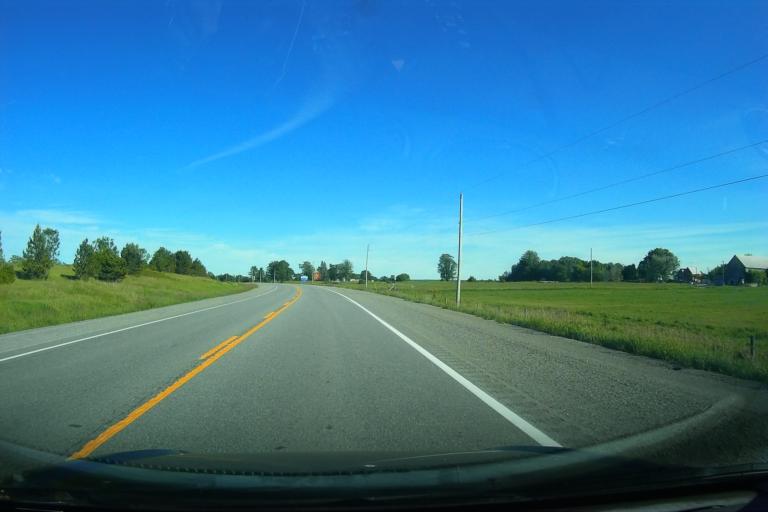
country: CA
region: Ontario
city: Pembroke
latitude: 45.6737
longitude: -76.9350
